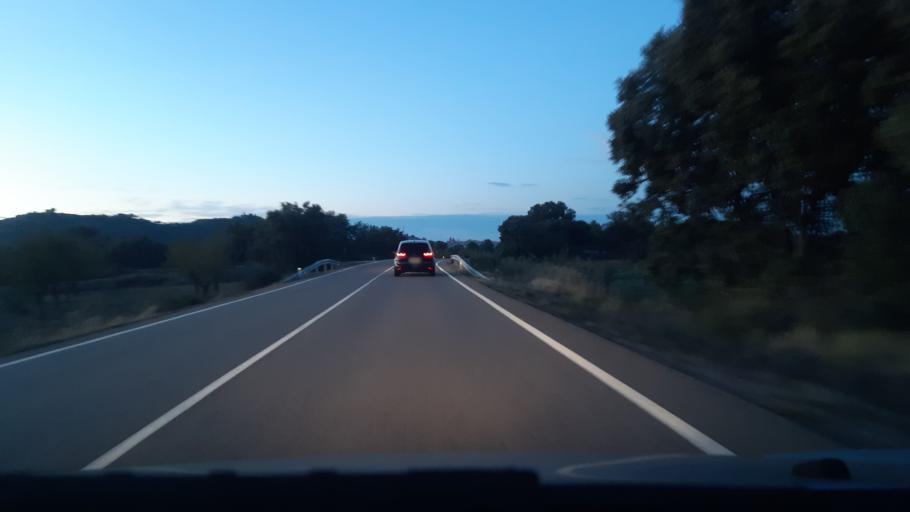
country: ES
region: Aragon
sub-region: Provincia de Teruel
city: Calaceite
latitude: 40.9967
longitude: 0.1962
